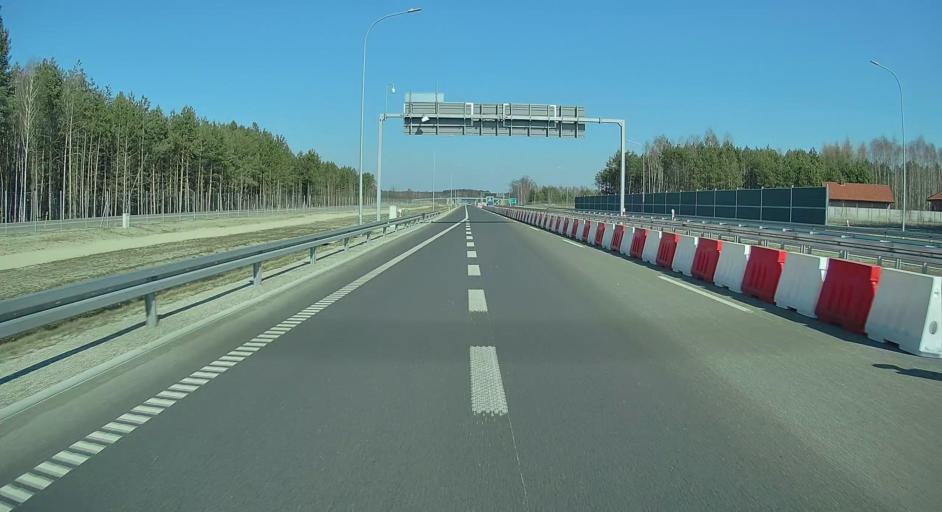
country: PL
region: Subcarpathian Voivodeship
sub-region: Powiat nizanski
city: Jarocin
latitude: 50.5778
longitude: 22.2511
